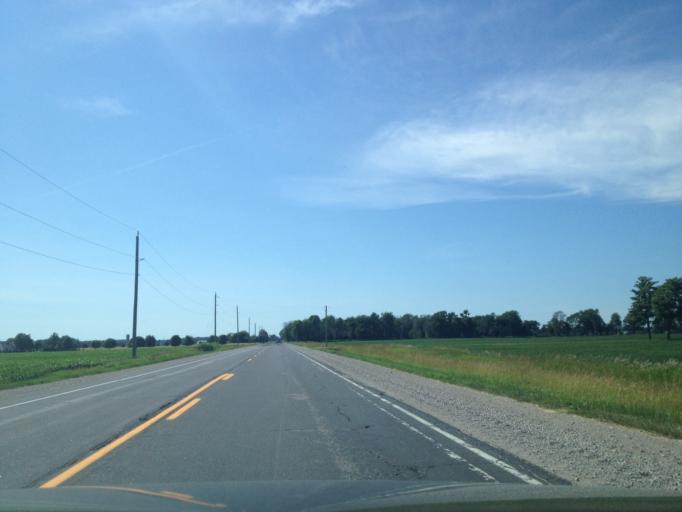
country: CA
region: Ontario
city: Stratford
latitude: 43.4911
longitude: -80.8522
